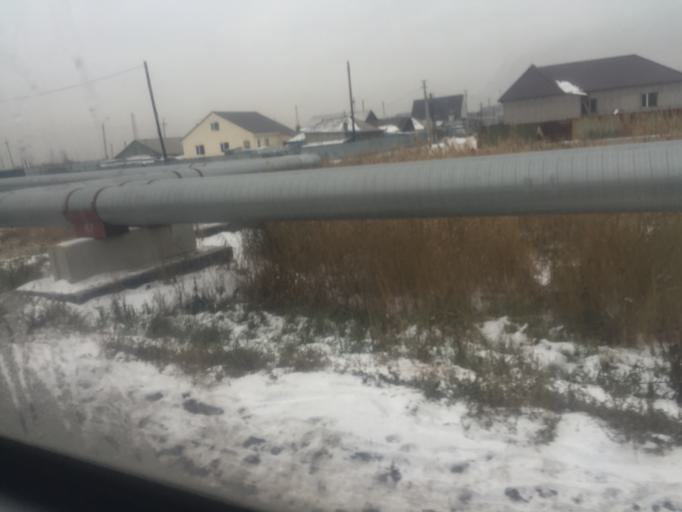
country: KZ
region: Astana Qalasy
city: Astana
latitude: 51.2081
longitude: 71.4039
